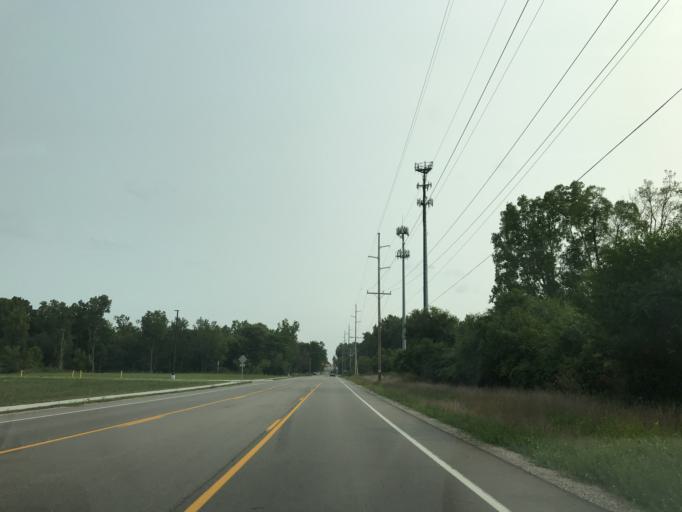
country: US
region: Michigan
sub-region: Ingham County
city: Okemos
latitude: 42.7501
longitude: -84.4476
